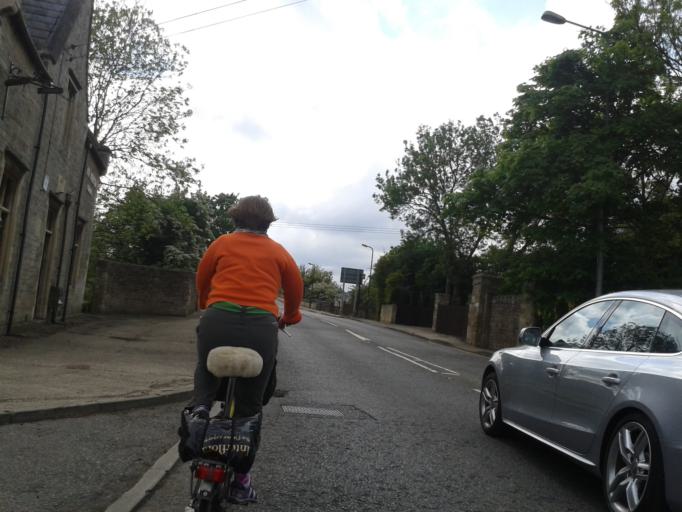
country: GB
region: England
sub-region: Northamptonshire
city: Oundle
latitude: 52.4884
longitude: -0.4599
